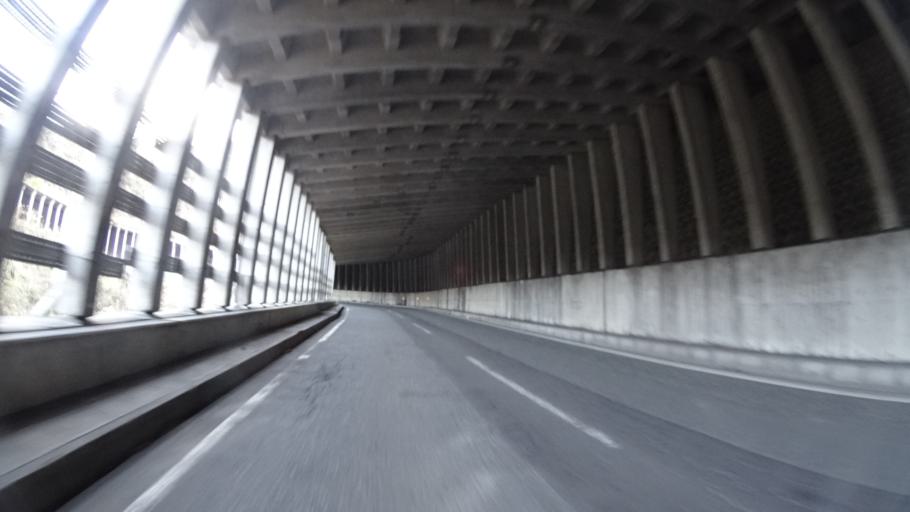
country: JP
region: Niigata
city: Shiozawa
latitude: 36.9855
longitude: 138.7800
